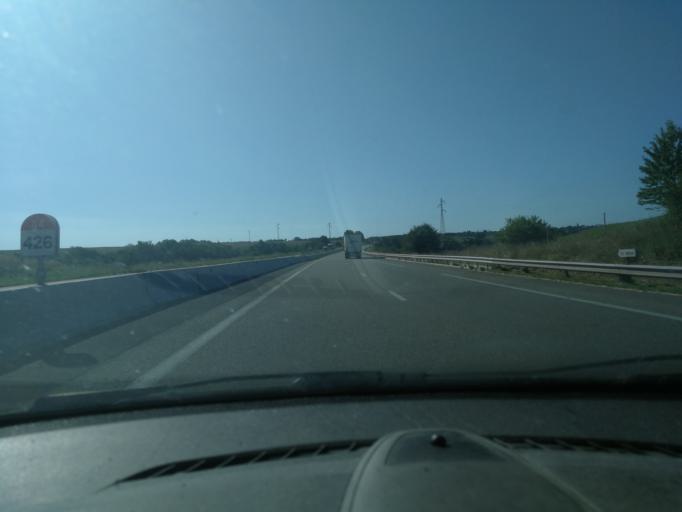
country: FR
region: Lorraine
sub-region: Departement de la Moselle
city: Phalsbourg
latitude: 48.7878
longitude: 7.2210
